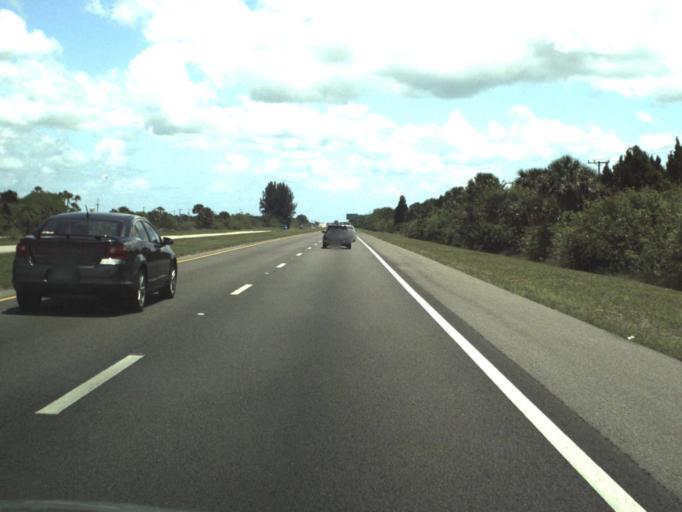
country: US
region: Florida
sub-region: Brevard County
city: Cocoa
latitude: 28.4051
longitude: -80.6835
